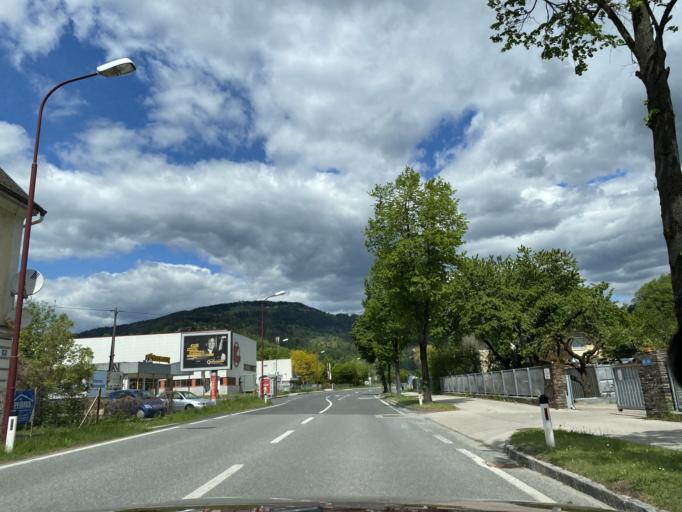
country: AT
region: Carinthia
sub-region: Politischer Bezirk Wolfsberg
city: Wolfsberg
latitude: 46.8480
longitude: 14.8448
